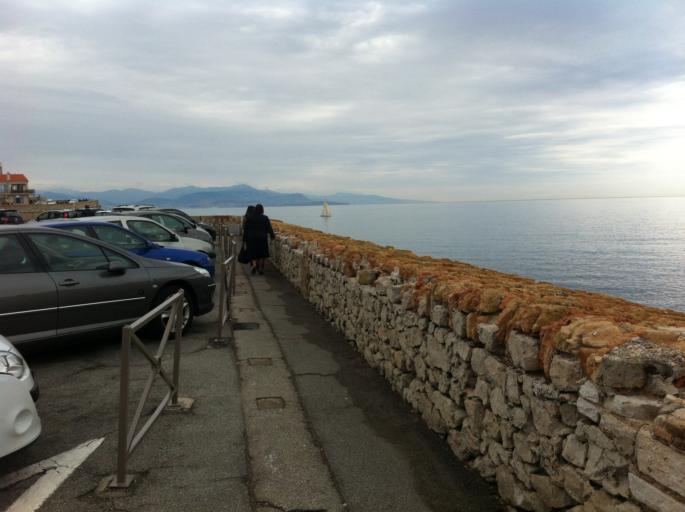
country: FR
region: Provence-Alpes-Cote d'Azur
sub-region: Departement des Alpes-Maritimes
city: Antibes
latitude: 43.5782
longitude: 7.1265
